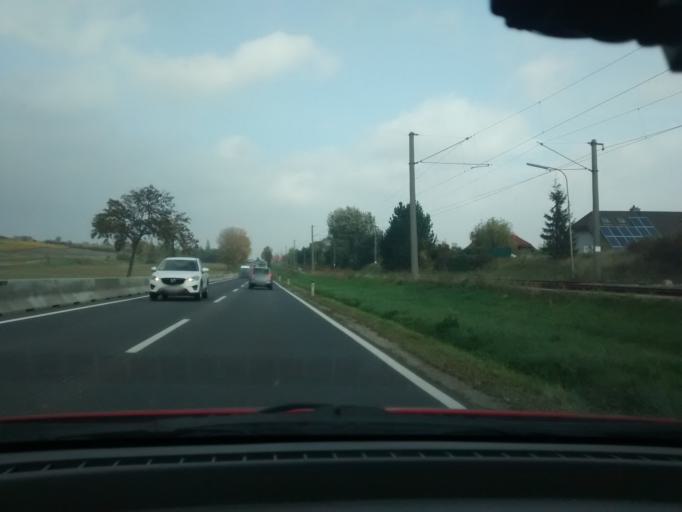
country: AT
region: Lower Austria
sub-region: Politischer Bezirk Modling
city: Neu-Guntramsdorf
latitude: 48.0573
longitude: 16.3102
